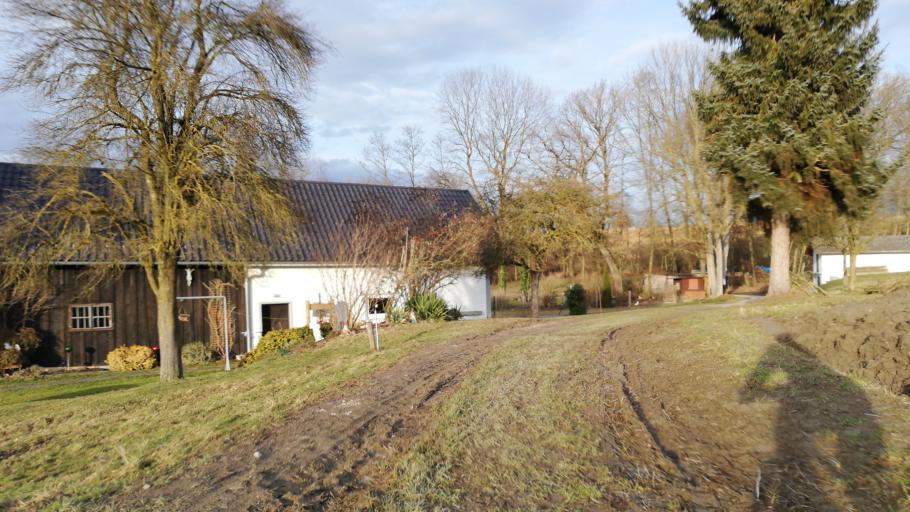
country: AT
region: Upper Austria
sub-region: Politischer Bezirk Grieskirchen
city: Bad Schallerbach
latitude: 48.2027
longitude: 13.9305
